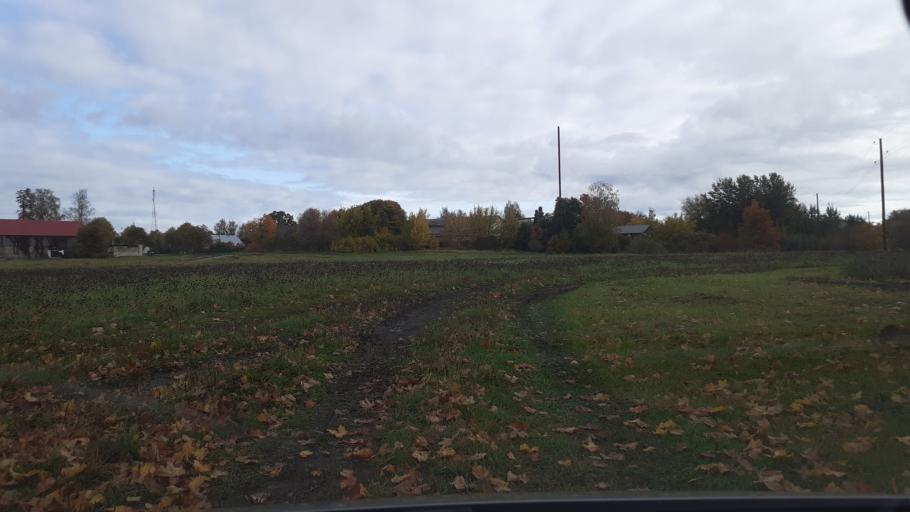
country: LV
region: Kuldigas Rajons
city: Kuldiga
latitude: 56.9693
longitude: 21.9853
